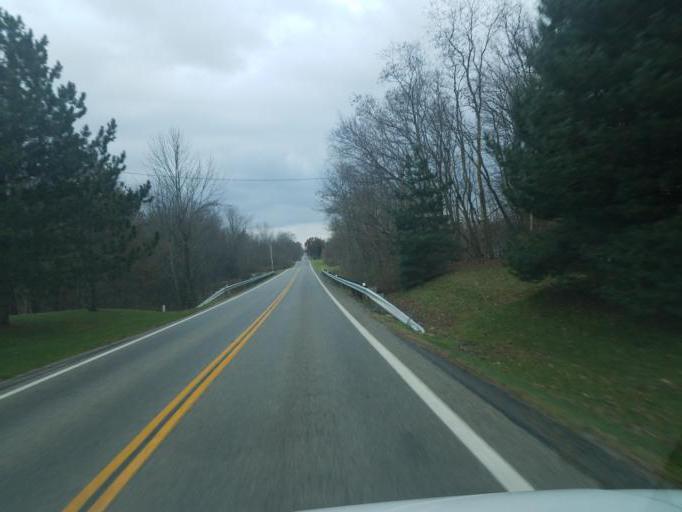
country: US
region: Ohio
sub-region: Morrow County
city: Mount Gilead
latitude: 40.6325
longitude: -82.7657
